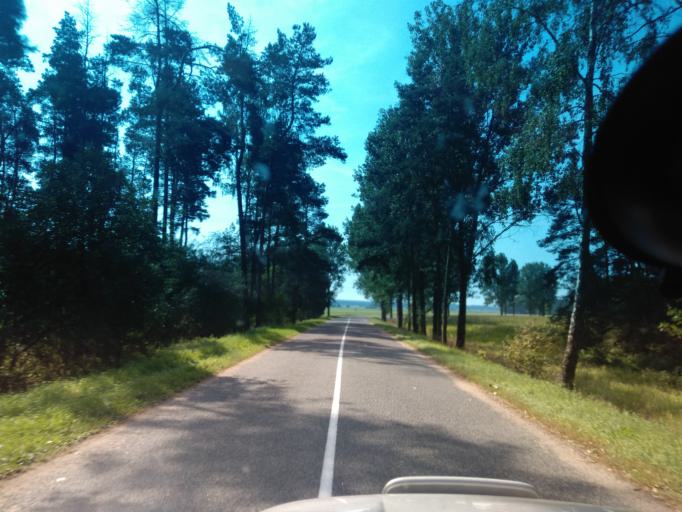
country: BY
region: Minsk
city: Kapyl'
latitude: 53.2735
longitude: 27.2300
